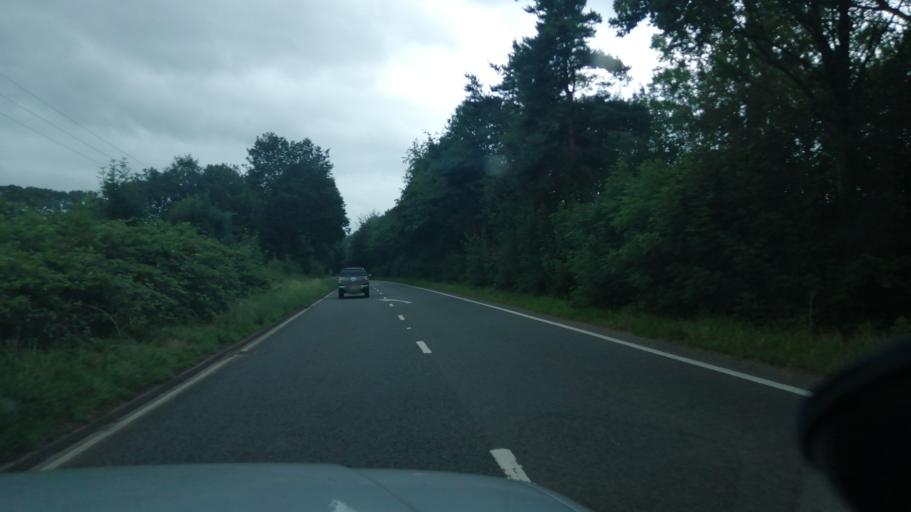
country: GB
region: Wales
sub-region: Monmouthshire
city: Abergavenny
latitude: 51.8143
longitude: -3.0082
